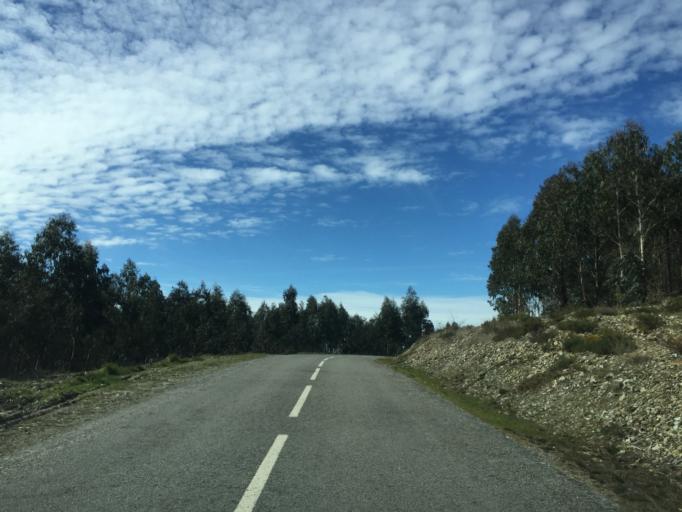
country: PT
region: Aveiro
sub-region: Arouca
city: Arouca
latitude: 40.9624
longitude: -8.2388
